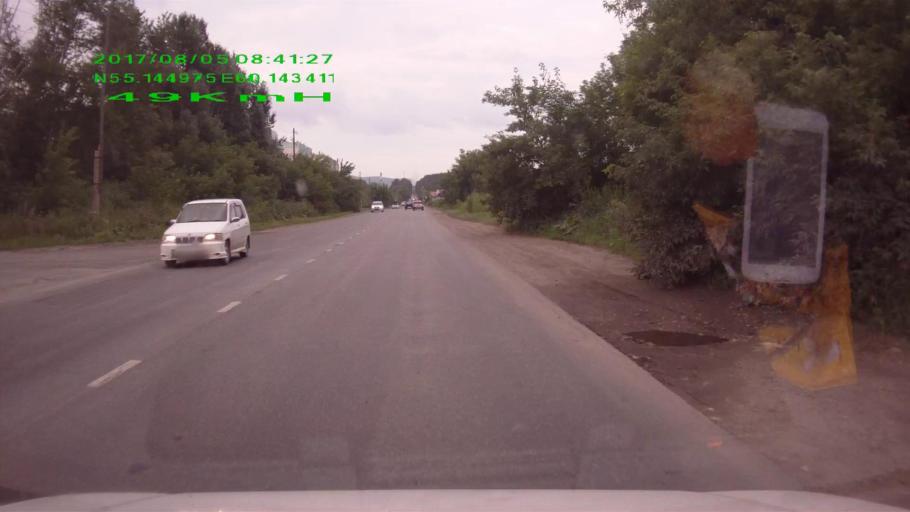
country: RU
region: Chelyabinsk
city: Turgoyak
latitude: 55.1447
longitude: 60.1434
